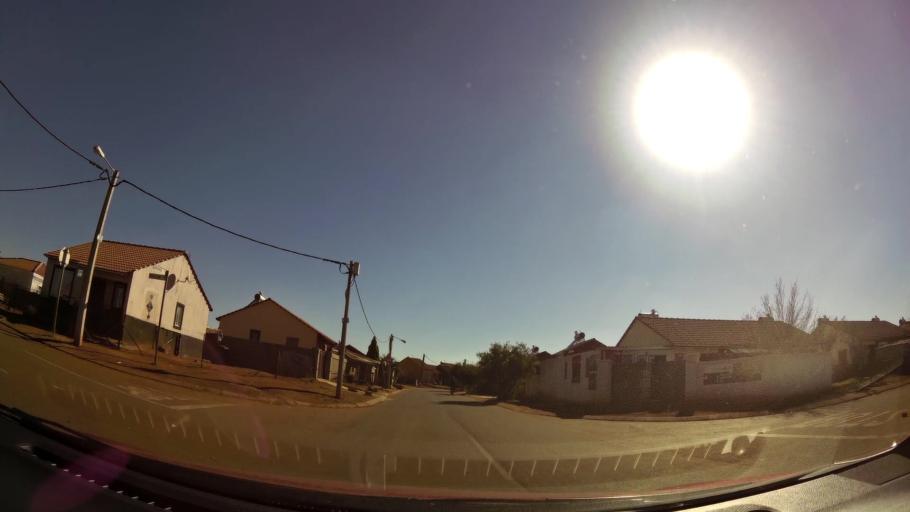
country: ZA
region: Gauteng
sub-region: City of Johannesburg Metropolitan Municipality
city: Soweto
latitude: -26.2389
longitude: 27.7980
